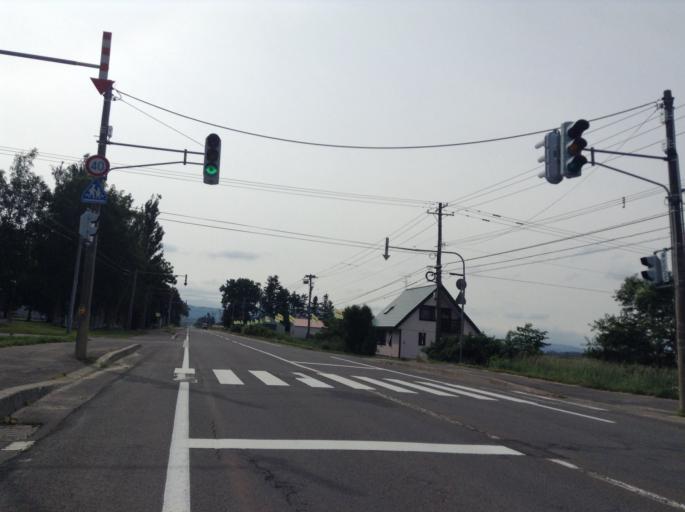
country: JP
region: Hokkaido
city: Nayoro
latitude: 44.4383
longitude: 142.3976
